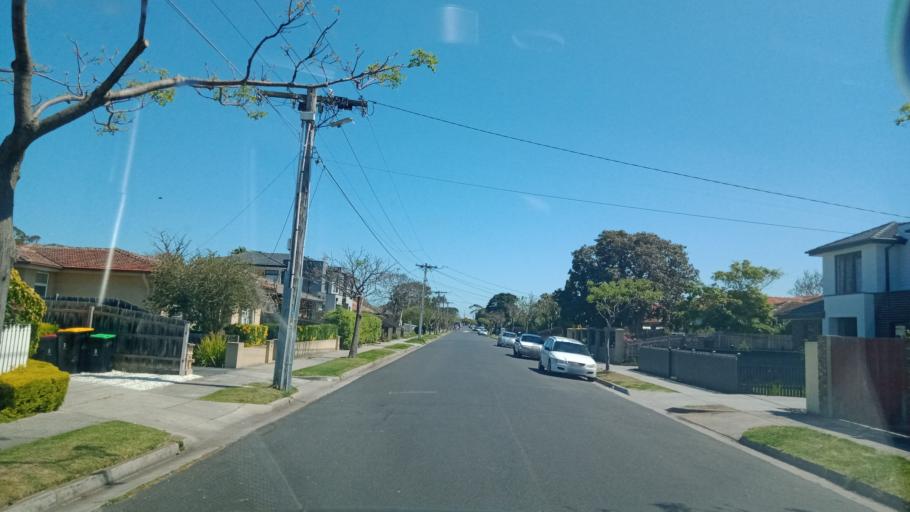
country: AU
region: Victoria
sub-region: Kingston
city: Chelsea
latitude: -38.0529
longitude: 145.1244
